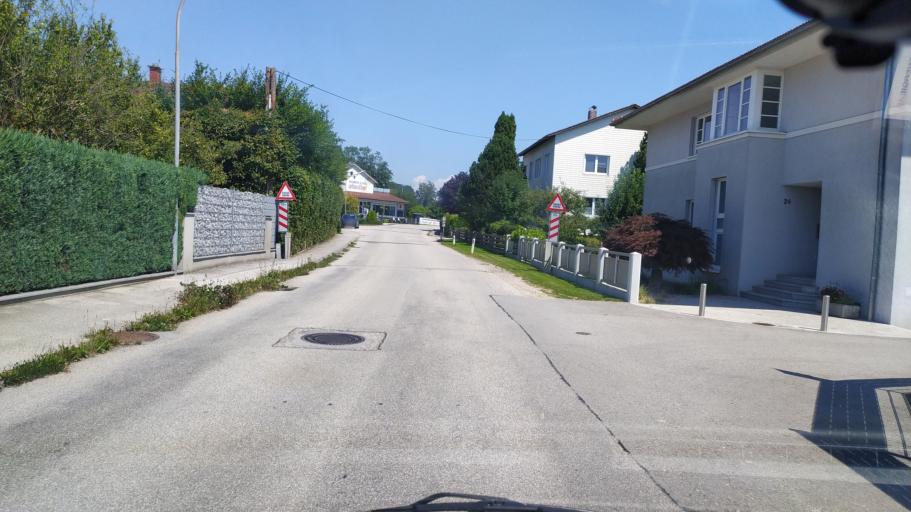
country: AT
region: Upper Austria
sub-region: Politischer Bezirk Linz-Land
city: Traun
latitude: 48.1407
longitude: 14.2356
